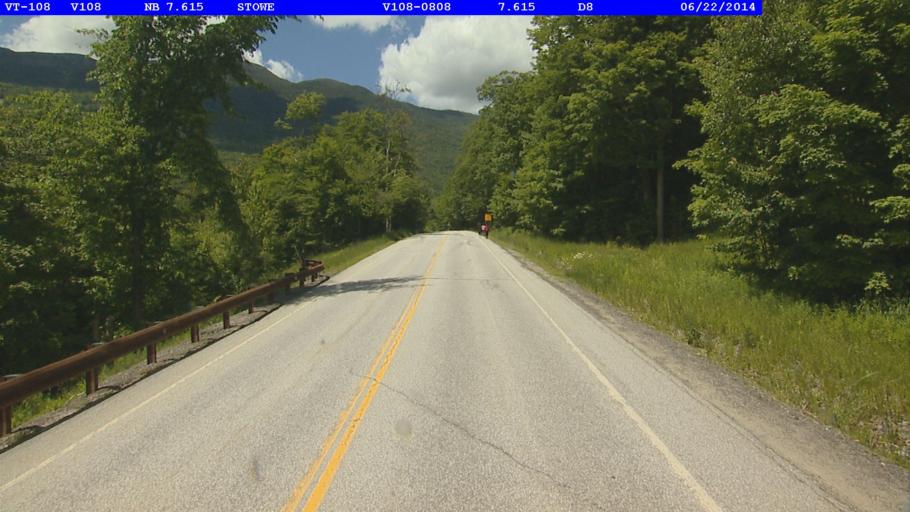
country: US
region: Vermont
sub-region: Lamoille County
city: Johnson
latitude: 44.5307
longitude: -72.7834
